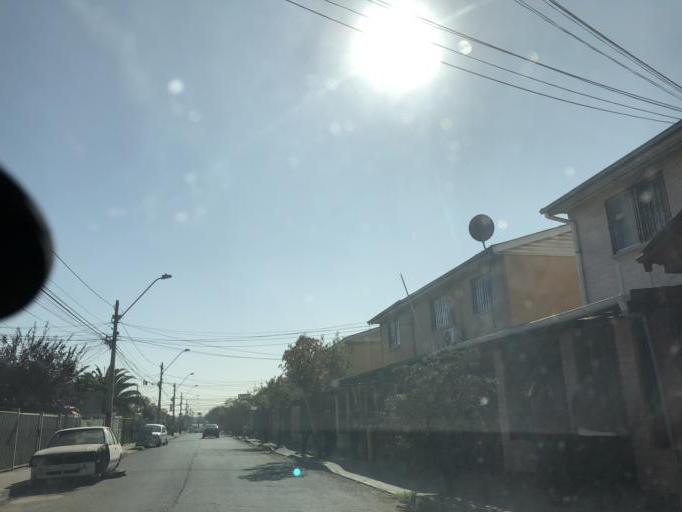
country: CL
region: Santiago Metropolitan
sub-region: Provincia de Cordillera
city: Puente Alto
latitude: -33.6117
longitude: -70.5938
